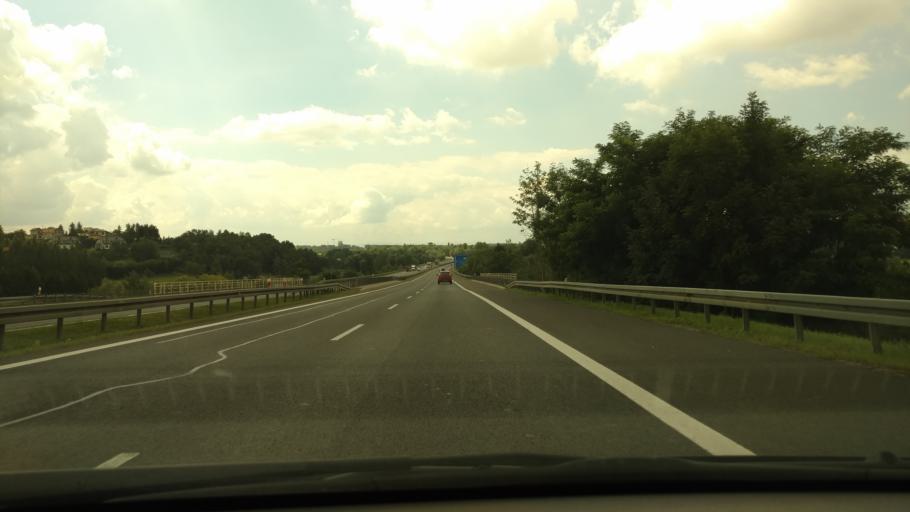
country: PL
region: Lesser Poland Voivodeship
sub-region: Powiat krakowski
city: Balice
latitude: 50.0937
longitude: 19.8165
